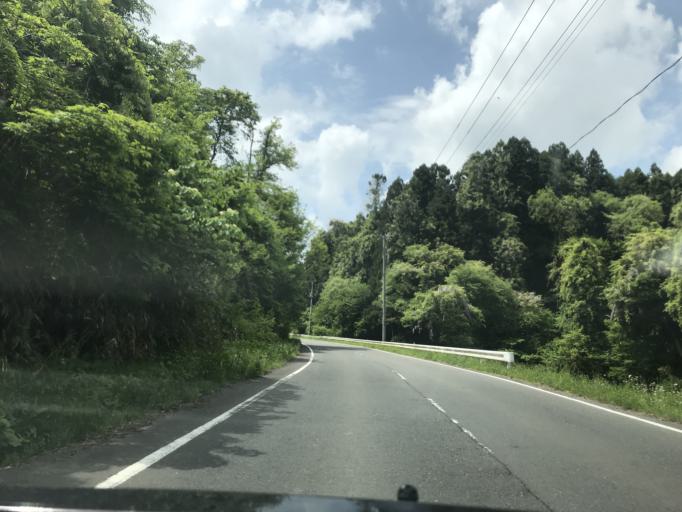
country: JP
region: Miyagi
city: Furukawa
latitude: 38.7364
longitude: 140.9281
